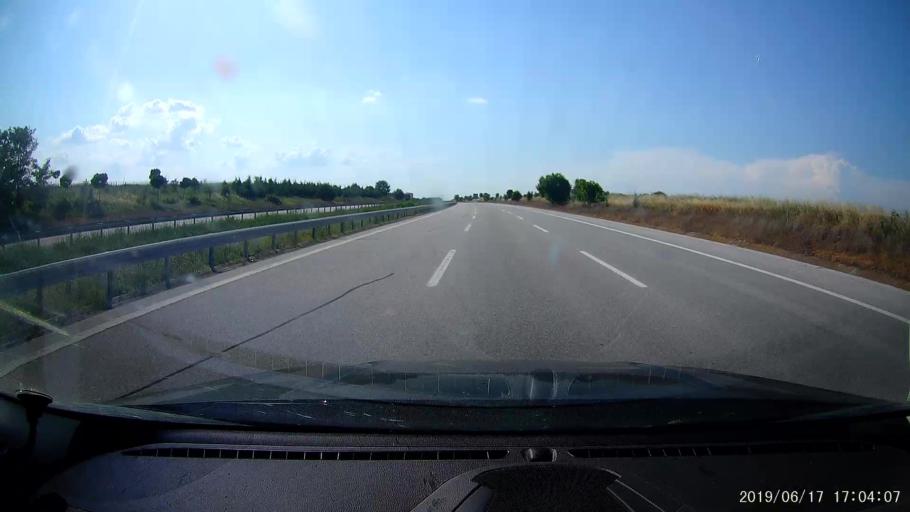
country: TR
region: Edirne
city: Haskoy
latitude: 41.6514
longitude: 26.7358
